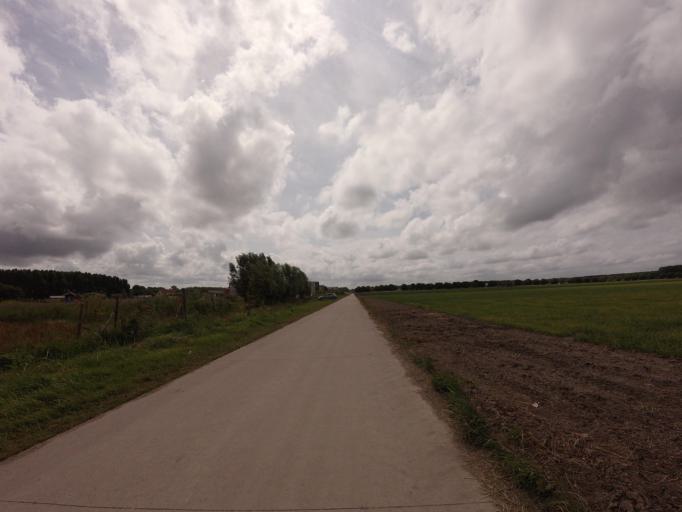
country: NL
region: Utrecht
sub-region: Gemeente Bunschoten
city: Spakenburg
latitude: 52.3358
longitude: 5.3299
